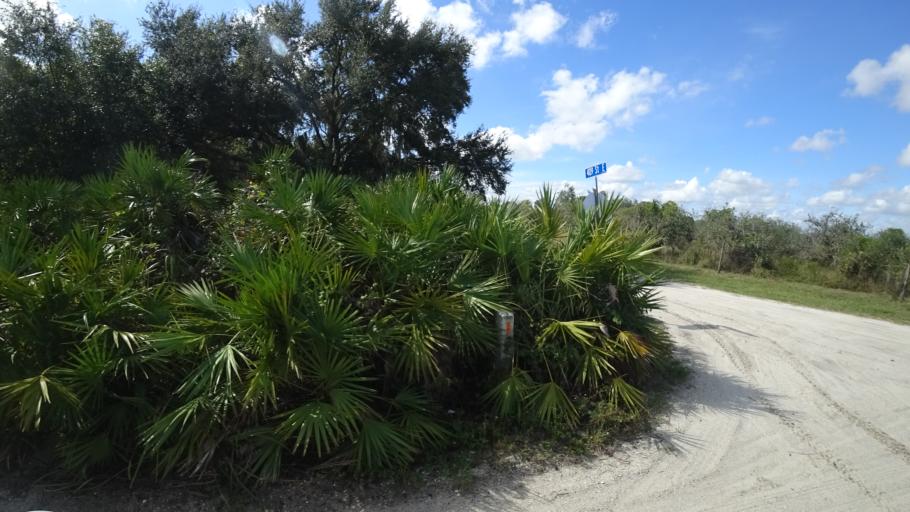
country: US
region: Florida
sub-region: DeSoto County
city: Arcadia
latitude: 27.3546
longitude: -82.1231
